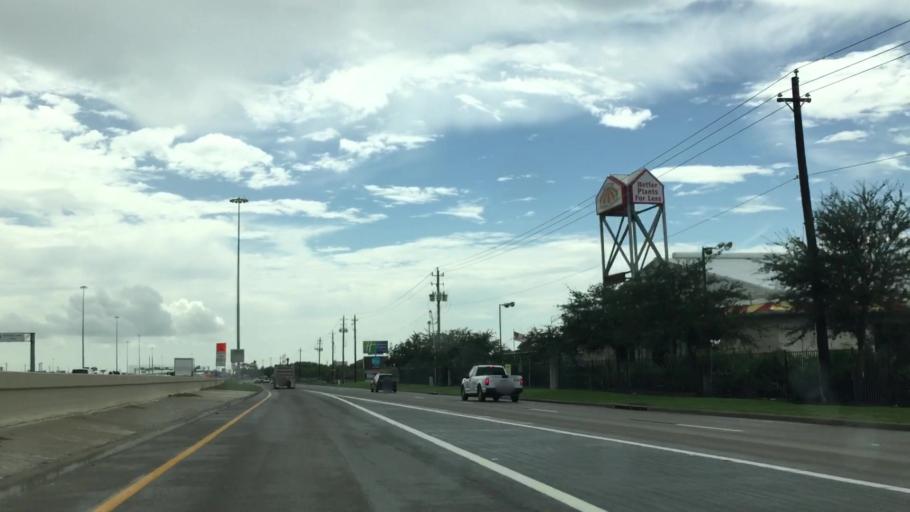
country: US
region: Texas
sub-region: Harris County
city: Webster
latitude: 29.5370
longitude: -95.1389
